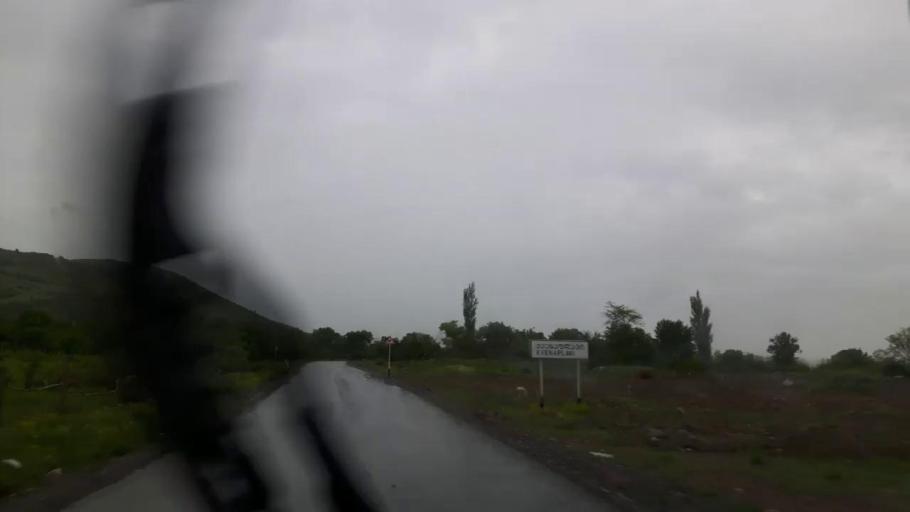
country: GE
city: Agara
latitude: 41.9815
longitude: 43.9431
